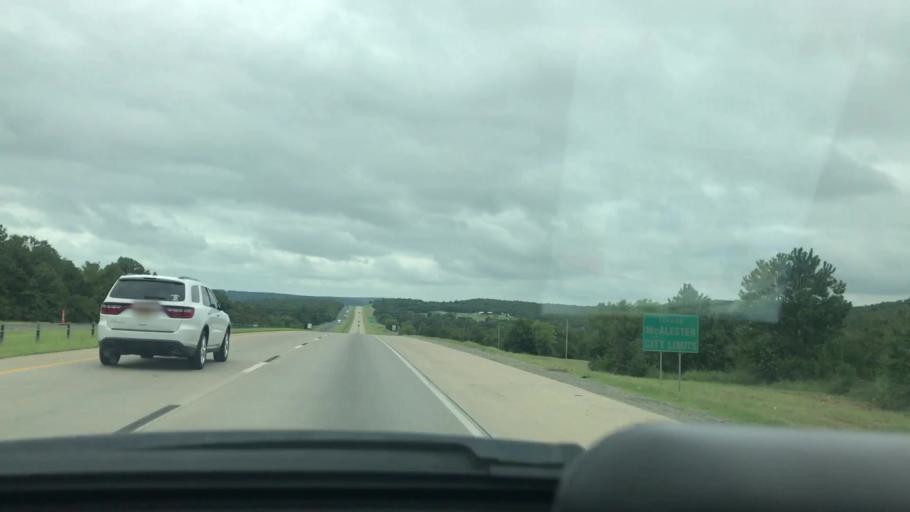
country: US
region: Oklahoma
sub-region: Pittsburg County
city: Krebs
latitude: 34.9712
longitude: -95.7236
